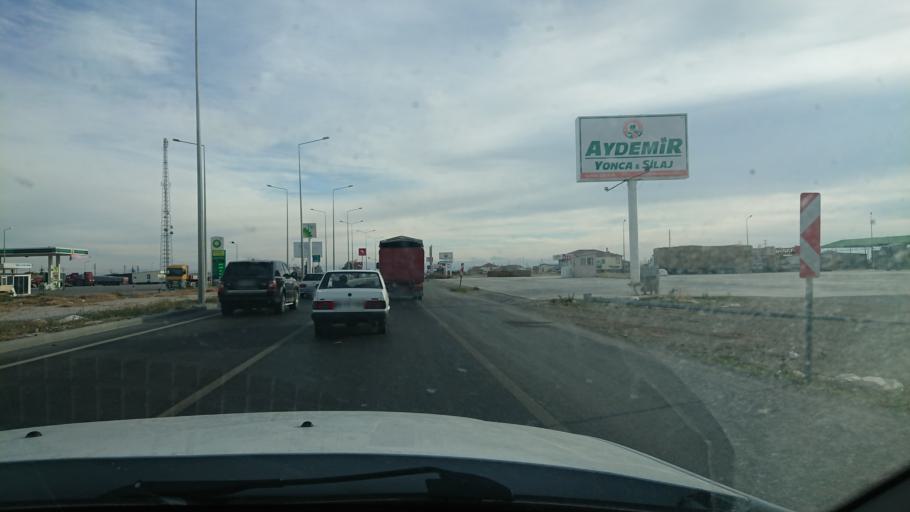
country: TR
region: Aksaray
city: Yesilova
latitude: 38.2912
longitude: 33.7614
